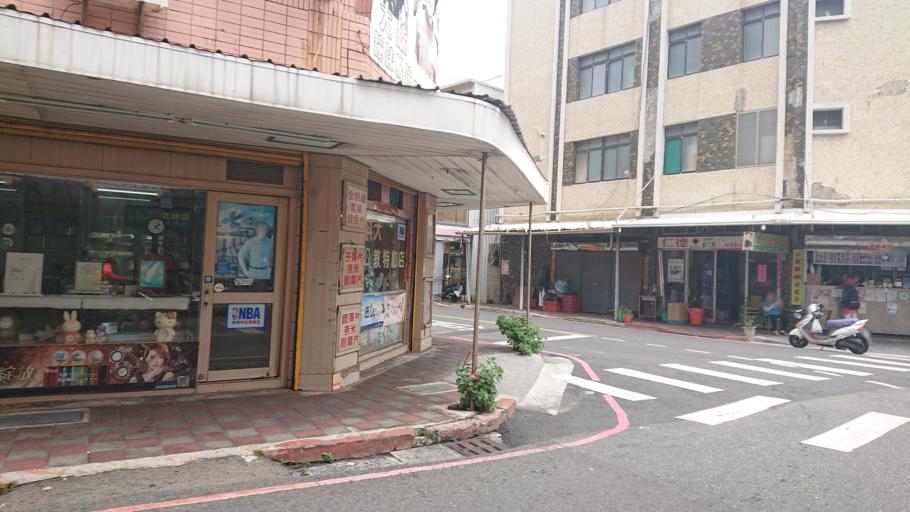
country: TW
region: Taiwan
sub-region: Penghu
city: Ma-kung
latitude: 23.5689
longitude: 119.5683
